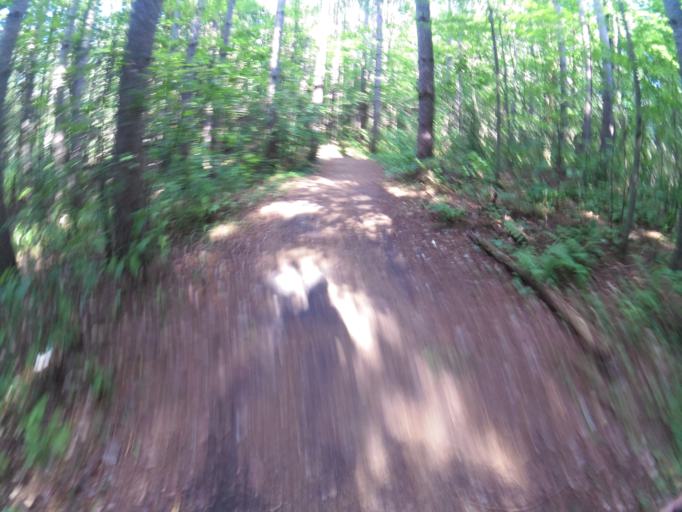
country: CA
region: Ontario
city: Ottawa
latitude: 45.3267
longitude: -75.7341
